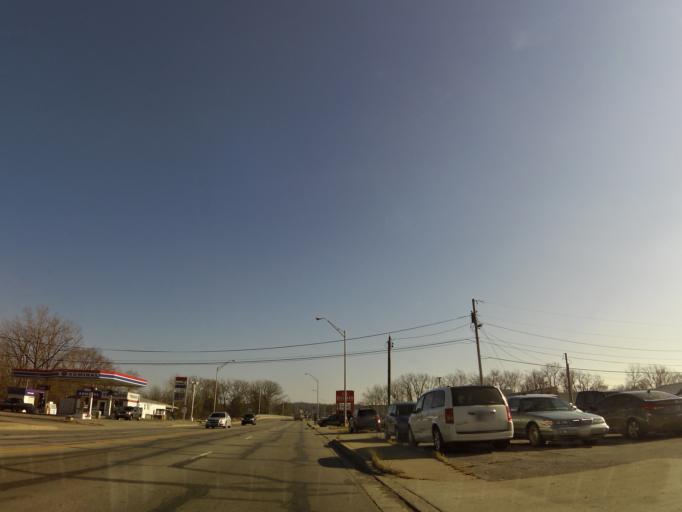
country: US
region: Indiana
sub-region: Fayette County
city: Connersville
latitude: 39.6397
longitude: -85.1335
